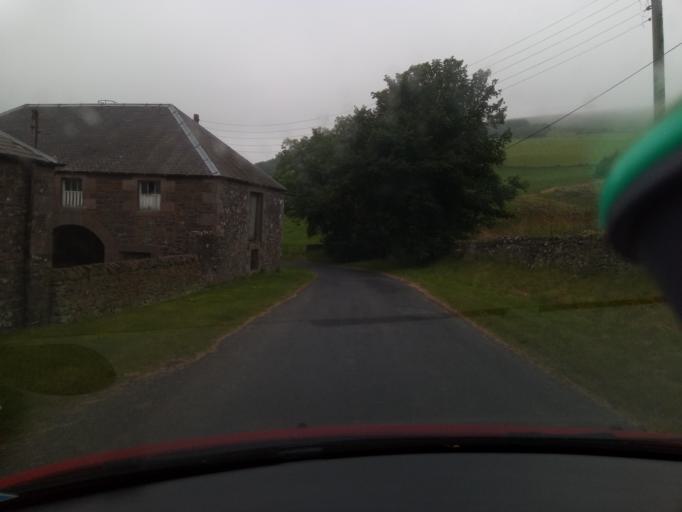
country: GB
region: Scotland
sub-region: The Scottish Borders
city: Galashiels
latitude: 55.6390
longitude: -2.8246
